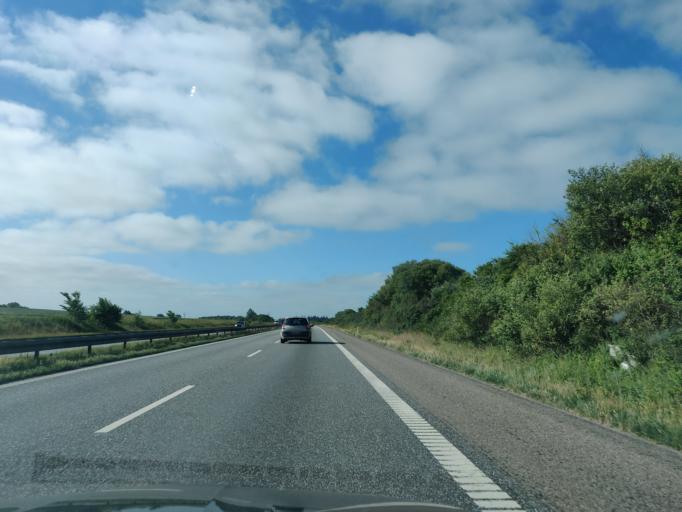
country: DK
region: North Denmark
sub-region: Mariagerfjord Kommune
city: Hobro
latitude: 56.7612
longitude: 9.6939
